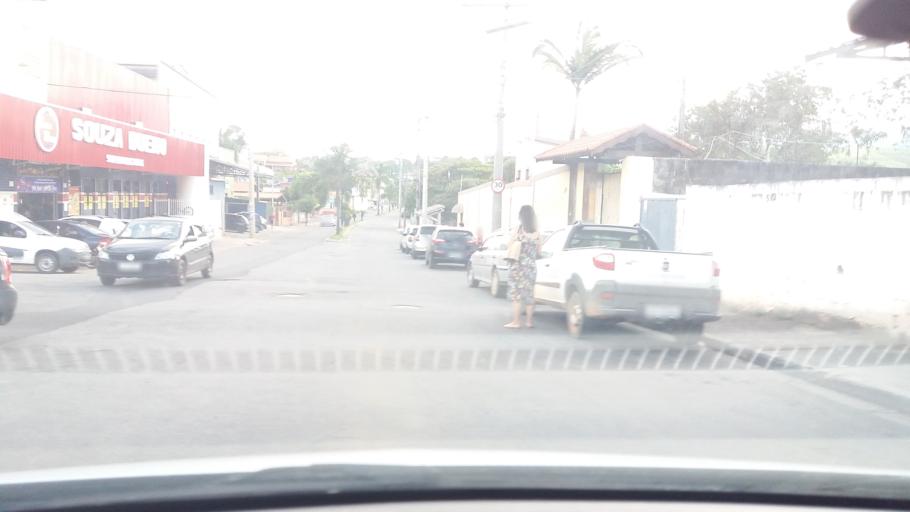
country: BR
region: Sao Paulo
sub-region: Bom Jesus Dos Perdoes
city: Bom Jesus dos Perdoes
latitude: -23.1413
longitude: -46.4676
